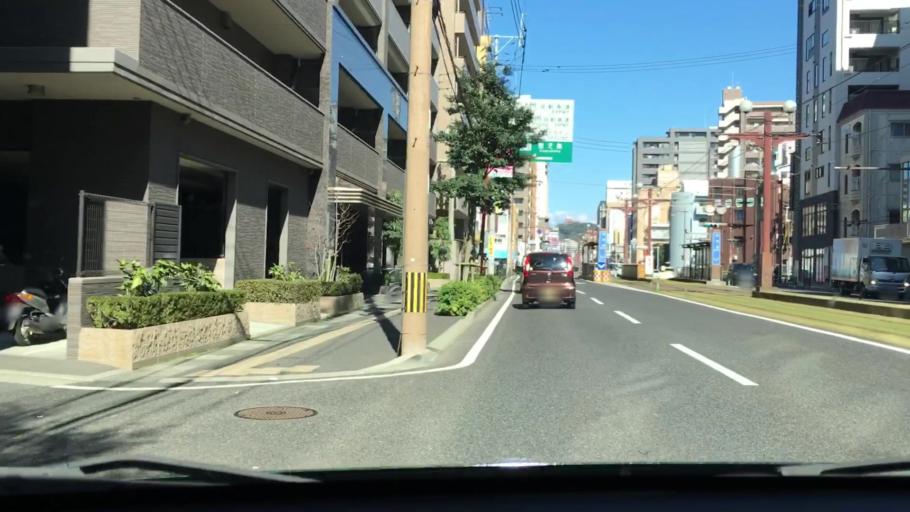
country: JP
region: Kagoshima
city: Kagoshima-shi
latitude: 31.5778
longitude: 130.5425
